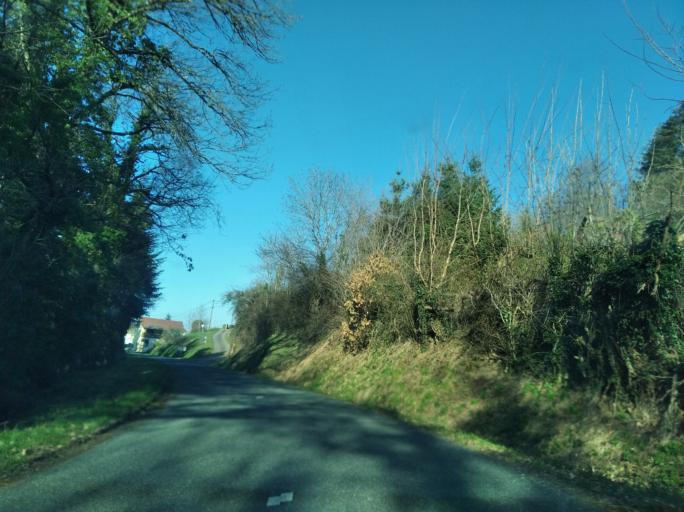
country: FR
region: Auvergne
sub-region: Departement de l'Allier
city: Le Mayet-de-Montagne
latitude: 46.1102
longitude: 3.6822
